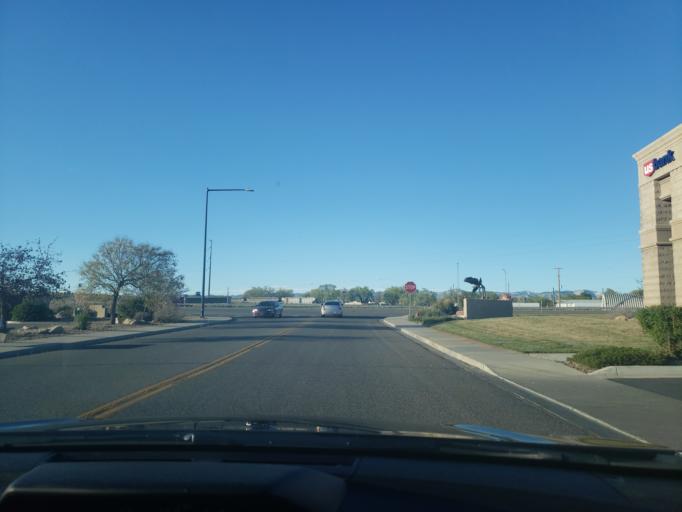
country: US
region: Colorado
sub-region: Mesa County
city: Fruita
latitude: 39.1534
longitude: -108.7350
